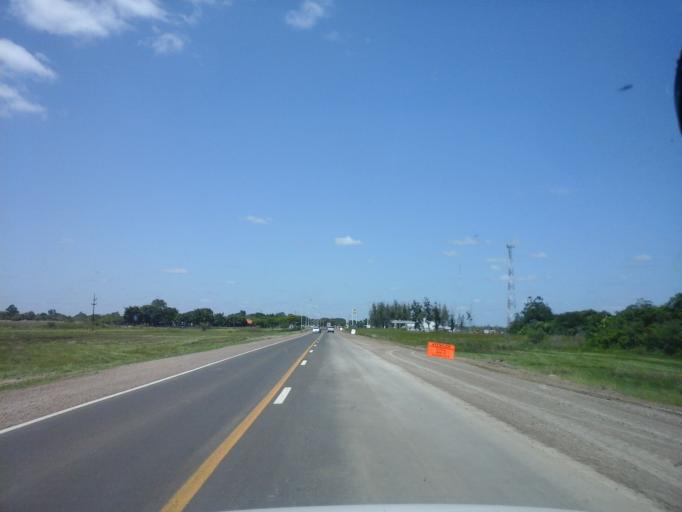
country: AR
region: Corrientes
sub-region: Departamento de Itati
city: Itati
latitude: -27.3492
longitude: -58.2345
